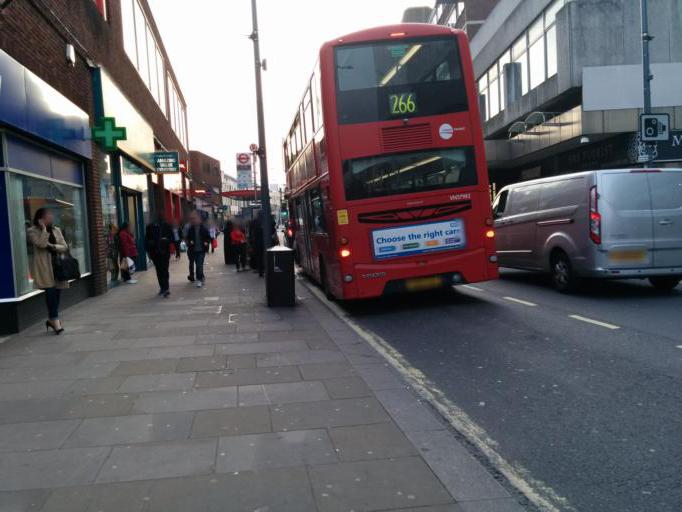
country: GB
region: England
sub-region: Greater London
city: Hammersmith
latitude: 51.4930
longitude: -0.2267
